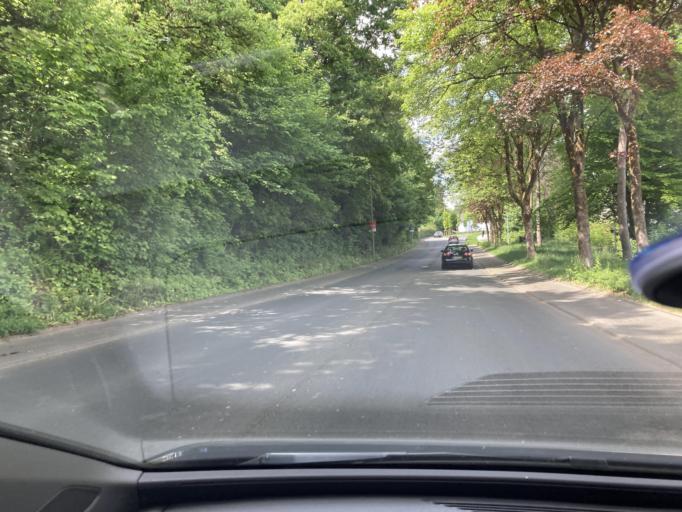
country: DE
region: North Rhine-Westphalia
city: Kreuztal
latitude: 50.9668
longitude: 7.9904
